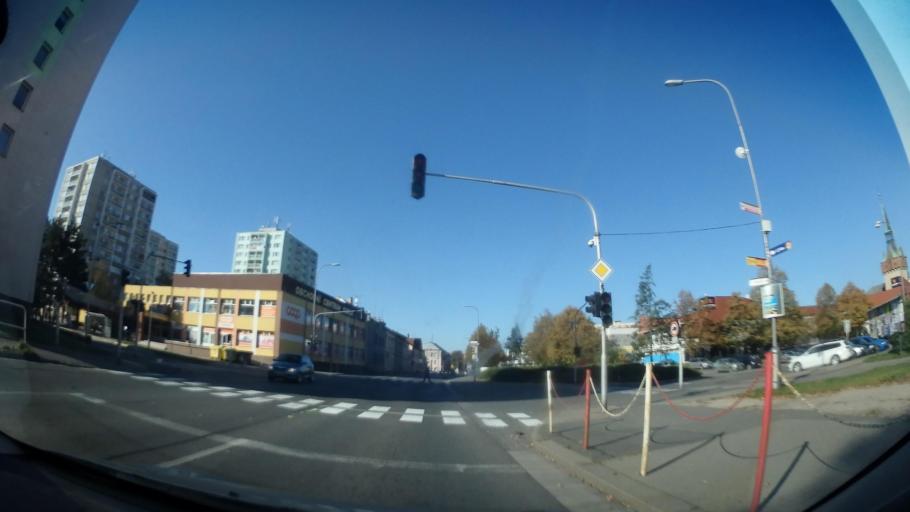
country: CZ
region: Pardubicky
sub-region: Okres Chrudim
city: Chrudim
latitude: 49.9467
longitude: 15.7929
